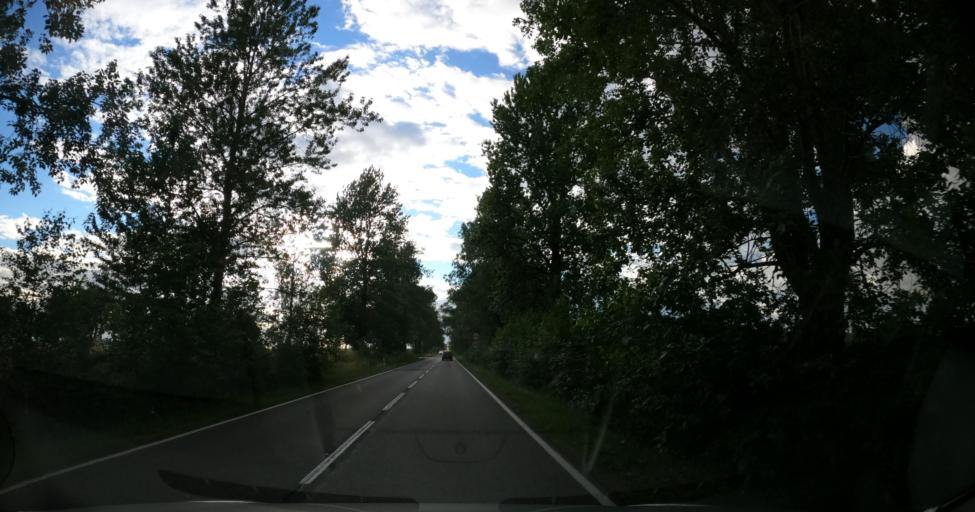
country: PL
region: Pomeranian Voivodeship
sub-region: Powiat slupski
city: Damnica
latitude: 54.4378
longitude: 17.3459
